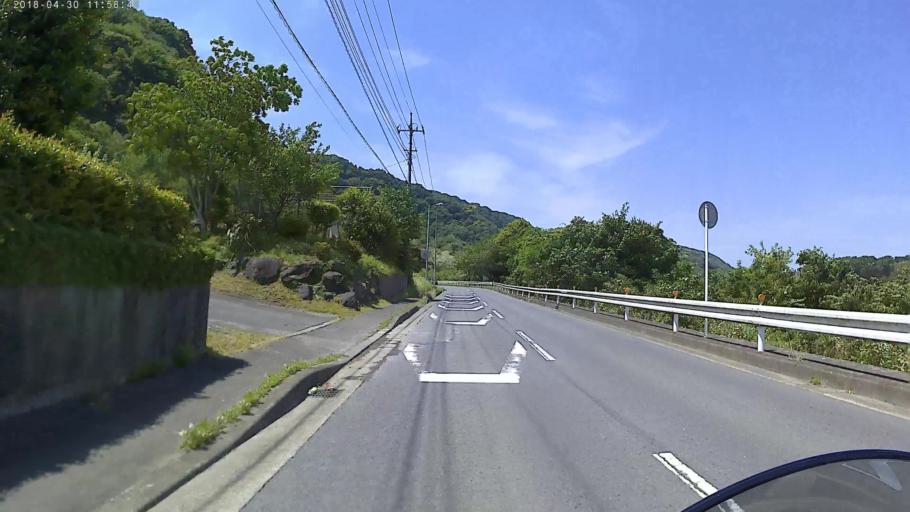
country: JP
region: Kanagawa
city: Zama
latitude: 35.5037
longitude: 139.3333
